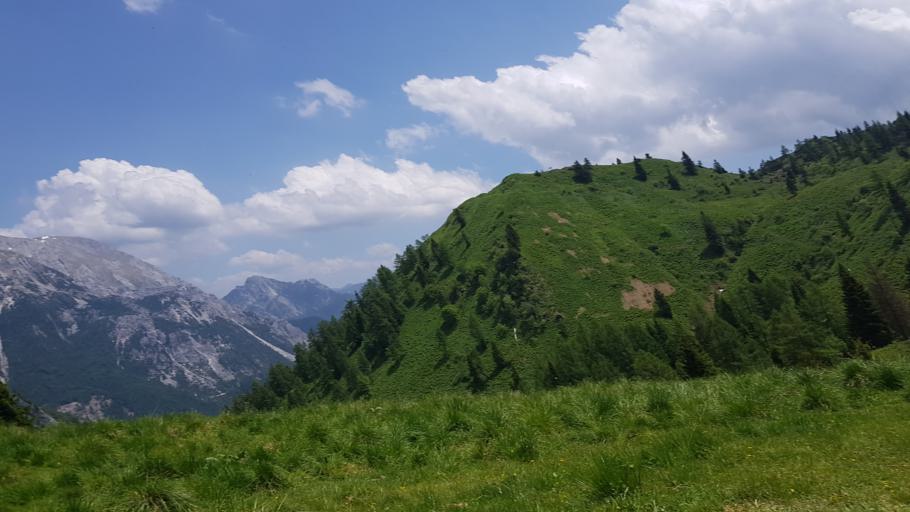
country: IT
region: Friuli Venezia Giulia
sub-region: Provincia di Udine
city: Paularo
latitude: 46.5244
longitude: 13.1812
